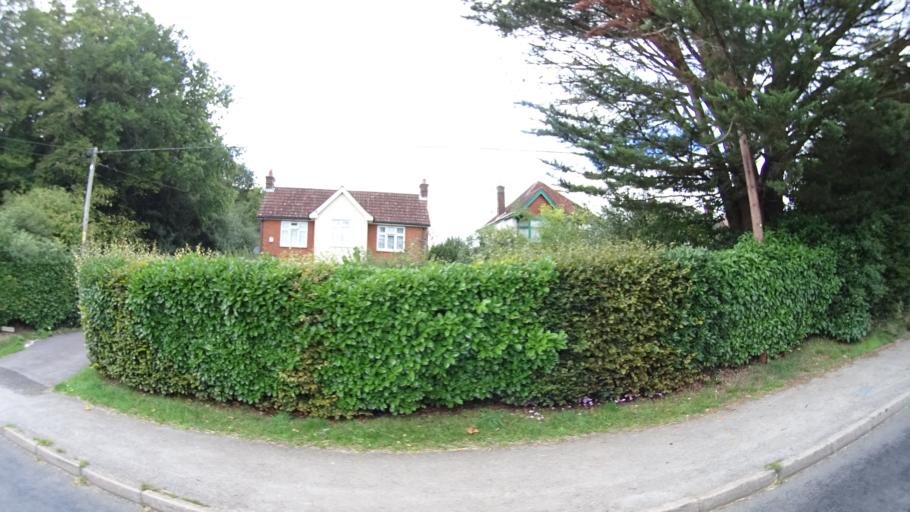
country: GB
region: England
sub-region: Hampshire
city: Romsey
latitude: 51.0140
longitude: -1.5454
